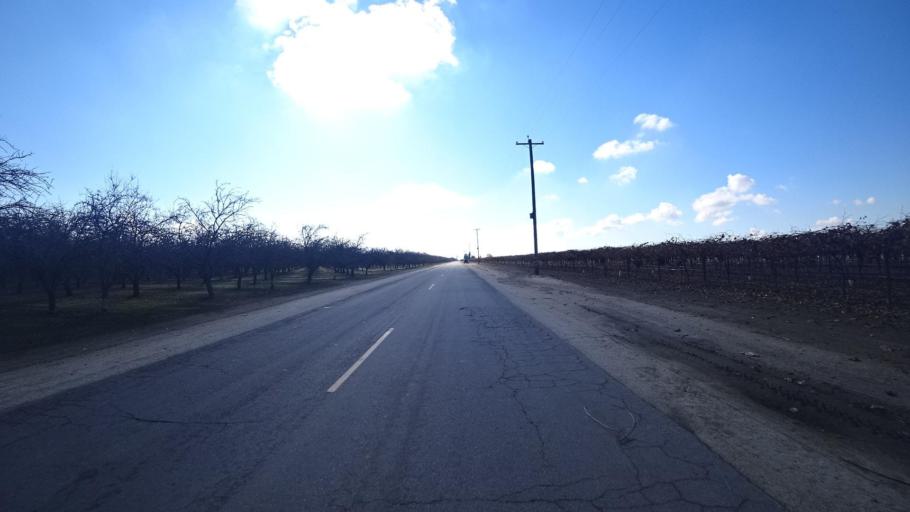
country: US
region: California
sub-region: Kern County
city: McFarland
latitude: 35.7100
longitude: -119.2586
